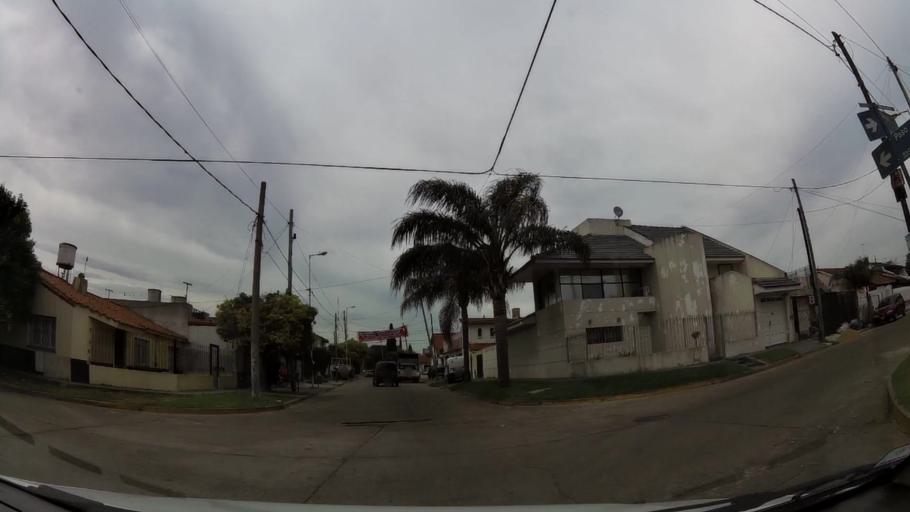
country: AR
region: Buenos Aires
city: San Justo
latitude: -34.6660
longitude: -58.5225
